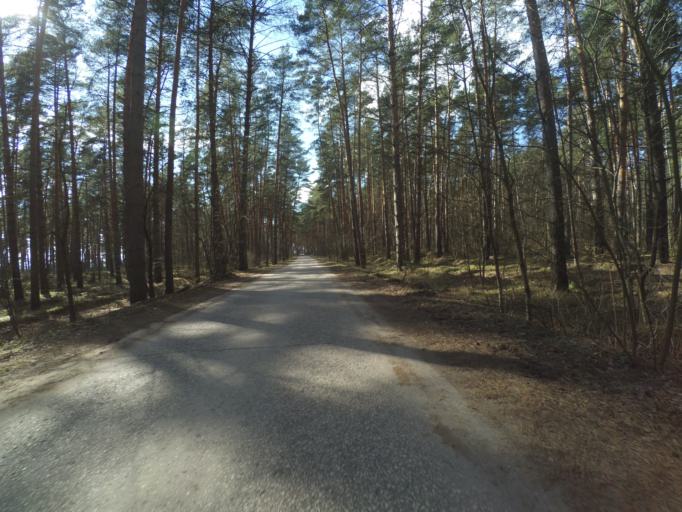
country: RU
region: Moskovskaya
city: Stupino
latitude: 54.8475
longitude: 37.9935
